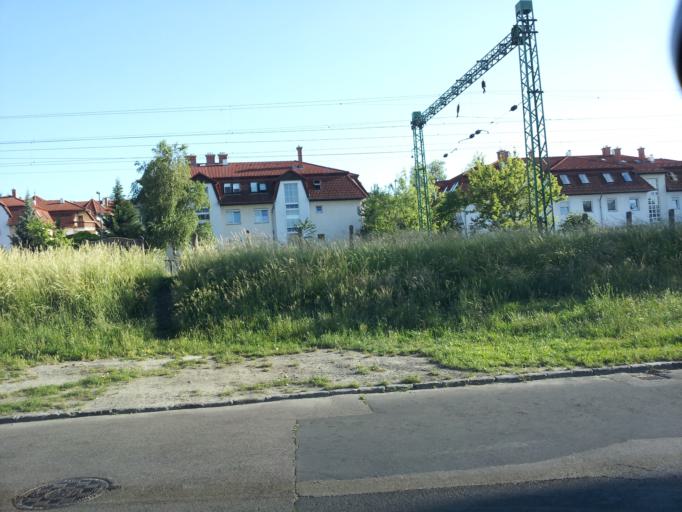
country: HU
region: Budapest
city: Budapest XIV. keruelet
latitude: 47.5324
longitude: 19.1235
